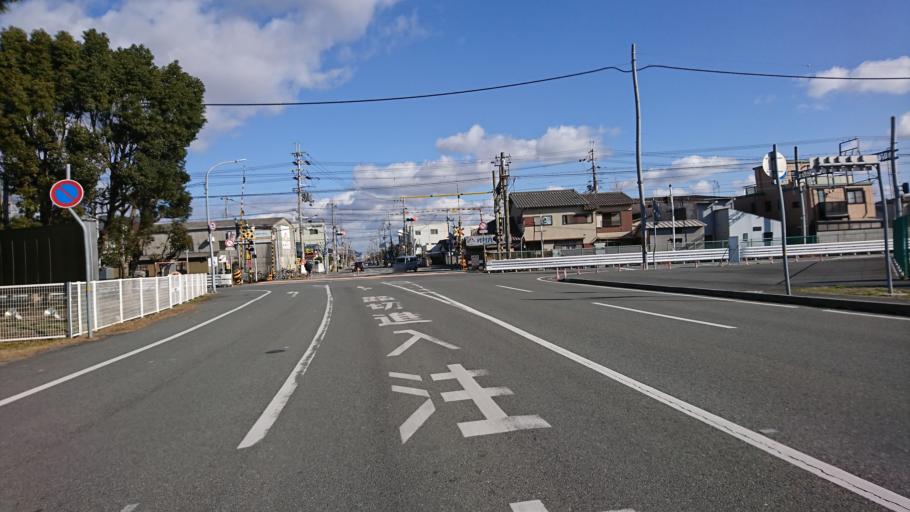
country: JP
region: Hyogo
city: Kakogawacho-honmachi
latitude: 34.7587
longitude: 134.7919
